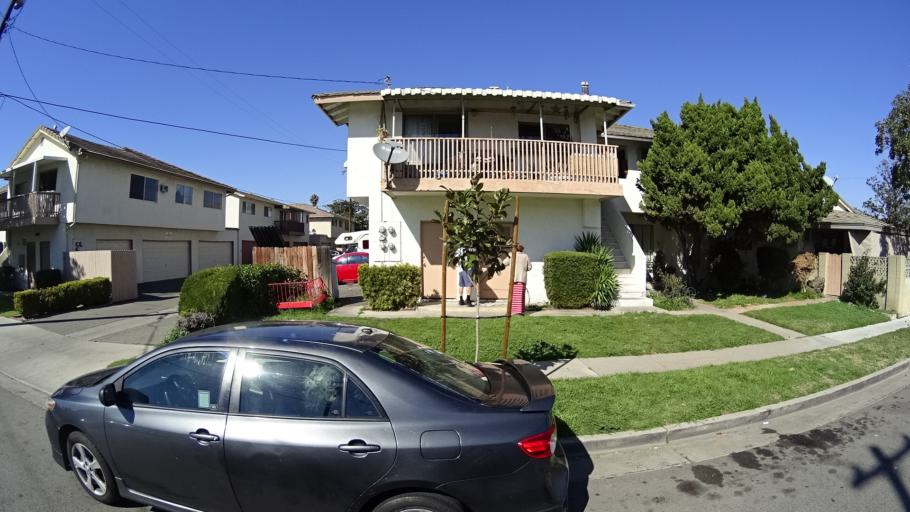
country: US
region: California
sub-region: Orange County
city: Anaheim
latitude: 33.8354
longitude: -117.9496
